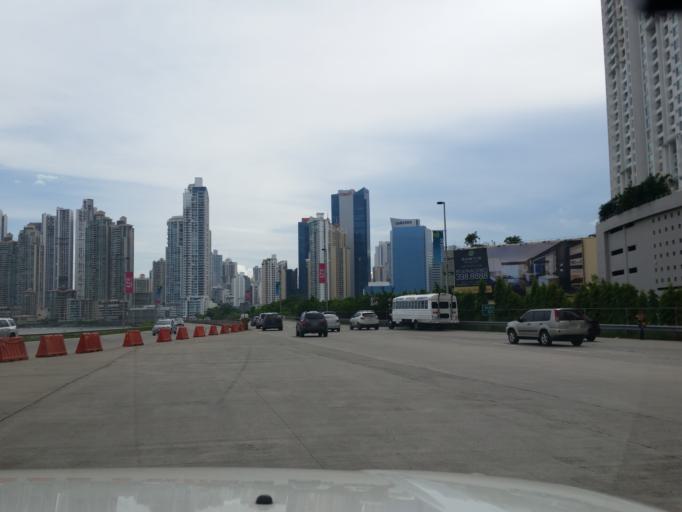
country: PA
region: Panama
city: Panama
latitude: 8.9865
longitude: -79.5006
